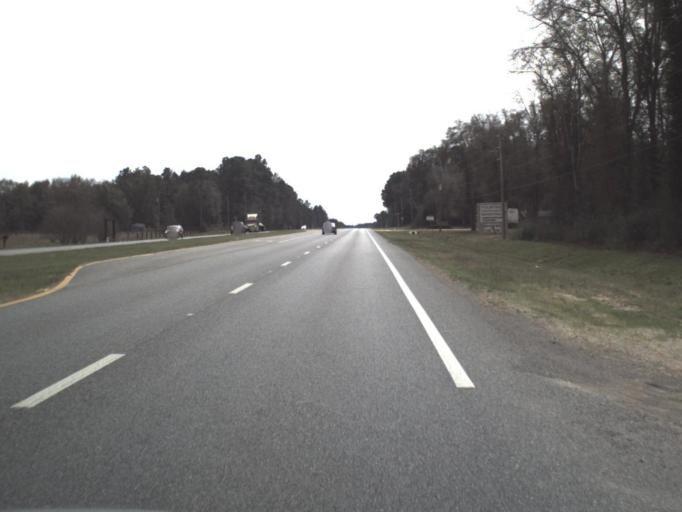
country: US
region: Florida
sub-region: Bay County
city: Youngstown
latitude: 30.5140
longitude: -85.4103
